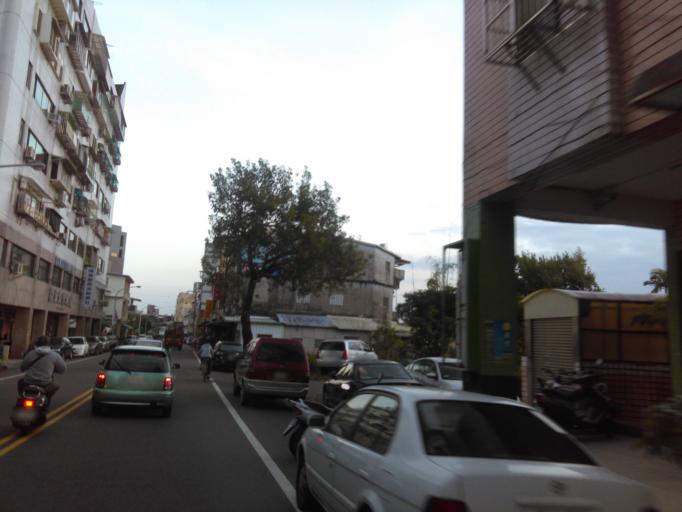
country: TW
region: Taiwan
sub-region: Yilan
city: Yilan
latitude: 24.8213
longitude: 121.7663
